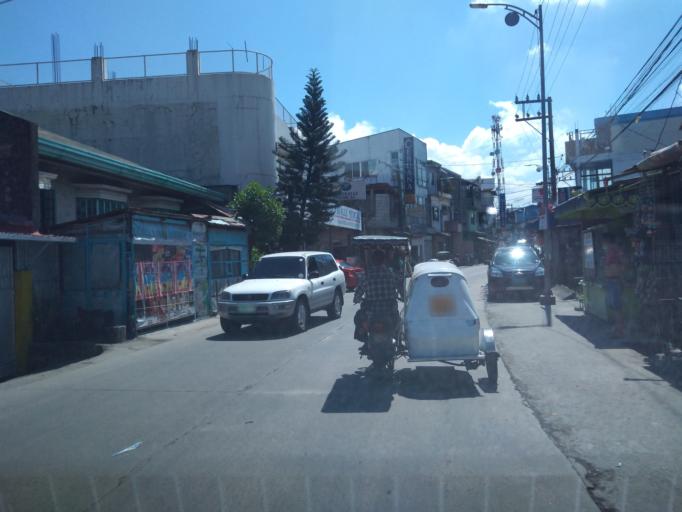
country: PH
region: Central Luzon
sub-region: Province of Bulacan
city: Bitungol
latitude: 14.8584
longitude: 121.0541
